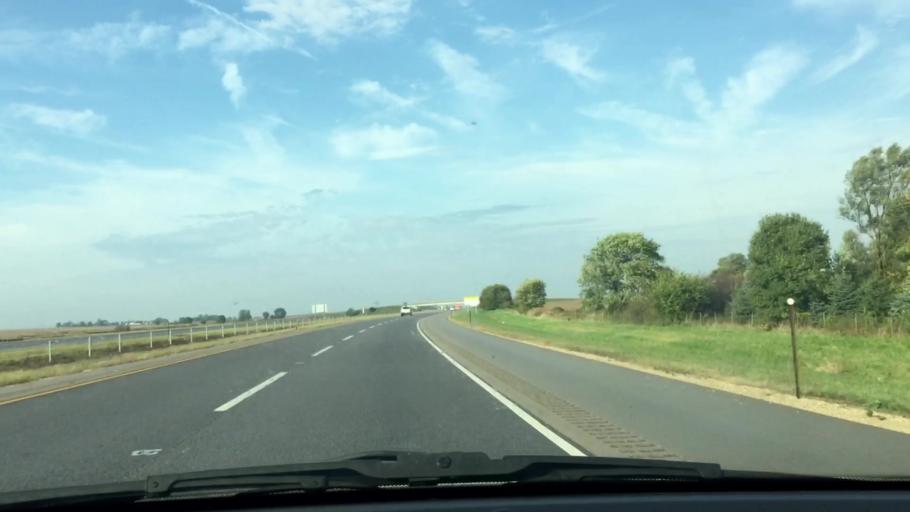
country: US
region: Illinois
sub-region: Ogle County
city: Rochelle
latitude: 41.8718
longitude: -89.1600
